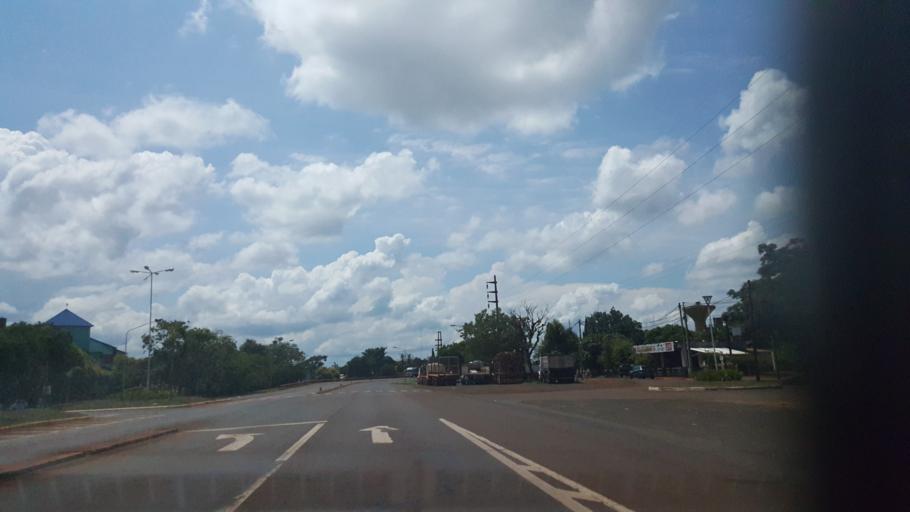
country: AR
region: Misiones
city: Puerto Rico
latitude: -26.8231
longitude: -55.0282
